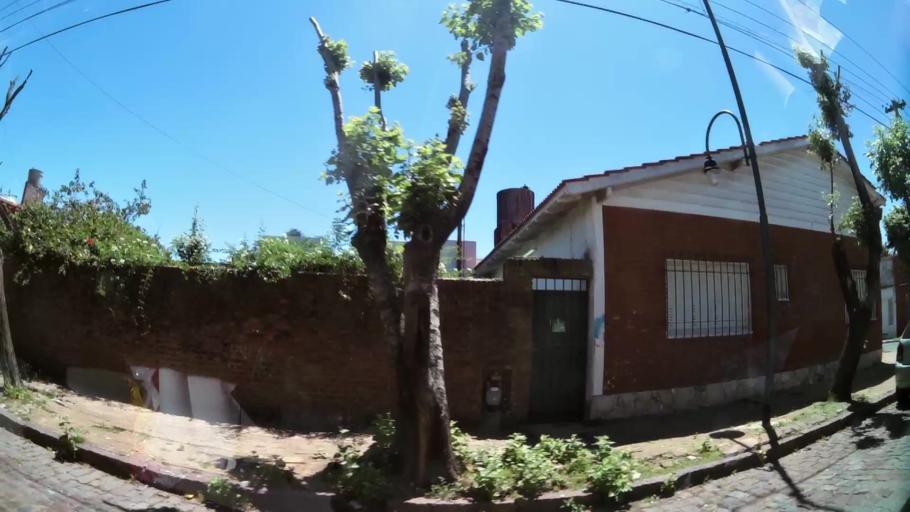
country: AR
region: Buenos Aires
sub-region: Partido de Tigre
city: Tigre
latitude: -34.4463
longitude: -58.5535
